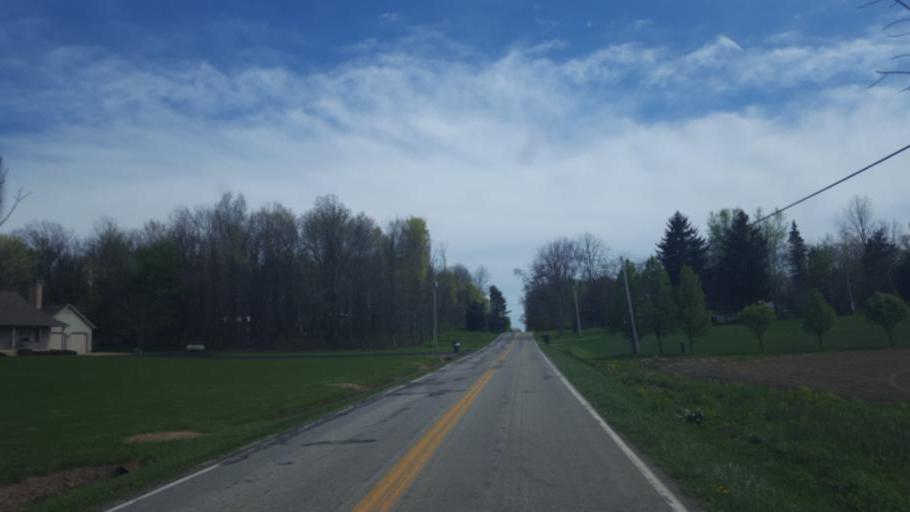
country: US
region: Ohio
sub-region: Richland County
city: Shelby
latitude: 40.8381
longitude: -82.6010
